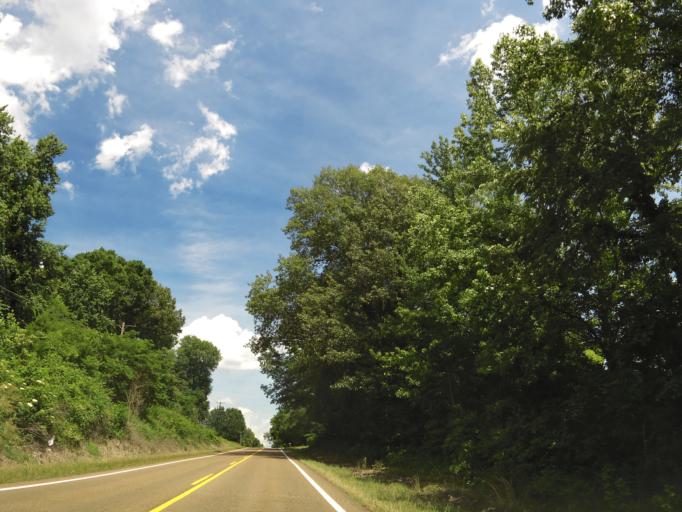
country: US
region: Tennessee
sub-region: Dyer County
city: Dyersburg
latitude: 36.0256
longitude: -89.3114
